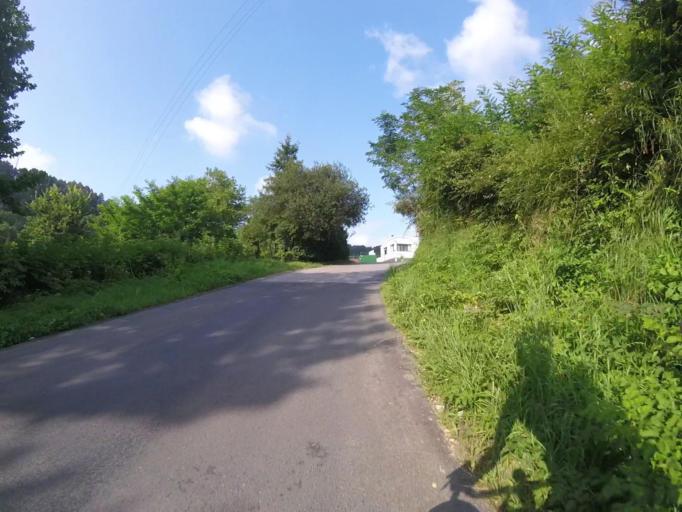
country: ES
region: Basque Country
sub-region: Provincia de Guipuzcoa
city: Astigarraga
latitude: 43.2592
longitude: -1.9524
